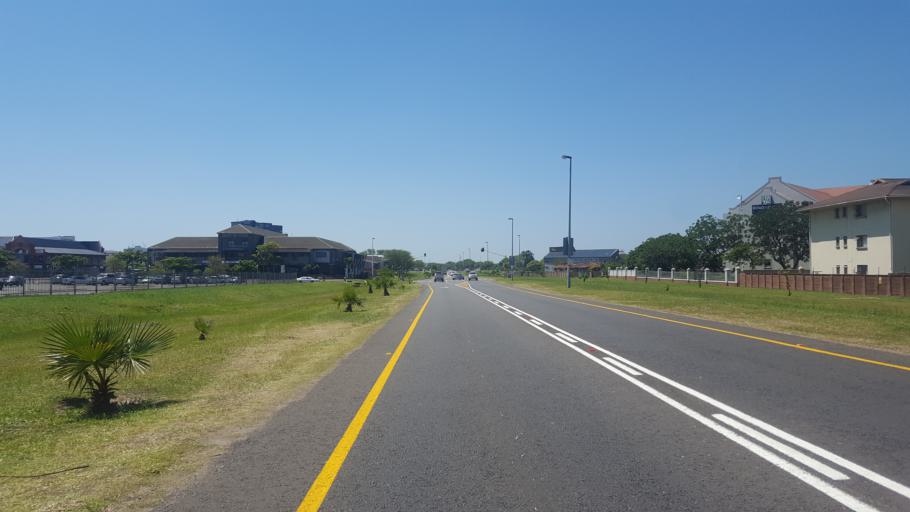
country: ZA
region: KwaZulu-Natal
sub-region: uThungulu District Municipality
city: Richards Bay
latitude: -28.7548
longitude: 32.0535
